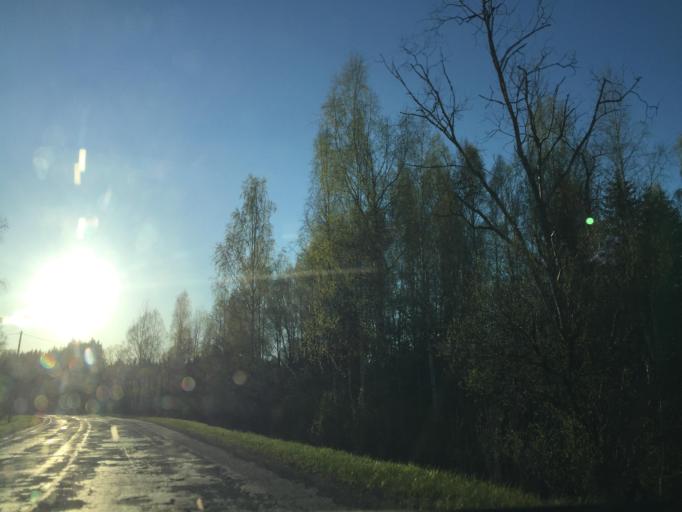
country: LV
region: Ergli
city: Ergli
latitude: 56.8790
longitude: 25.7384
